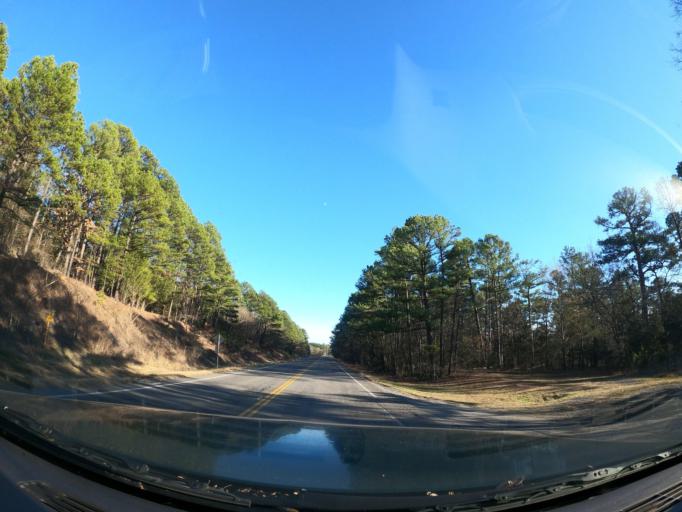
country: US
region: Oklahoma
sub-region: Latimer County
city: Wilburton
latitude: 34.9599
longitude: -95.3519
